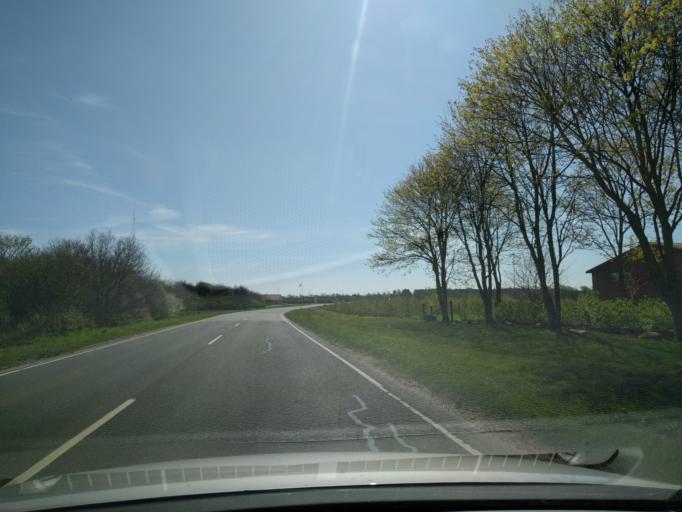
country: DK
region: Central Jutland
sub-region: Ringkobing-Skjern Kommune
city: Ringkobing
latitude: 56.1025
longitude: 8.2705
